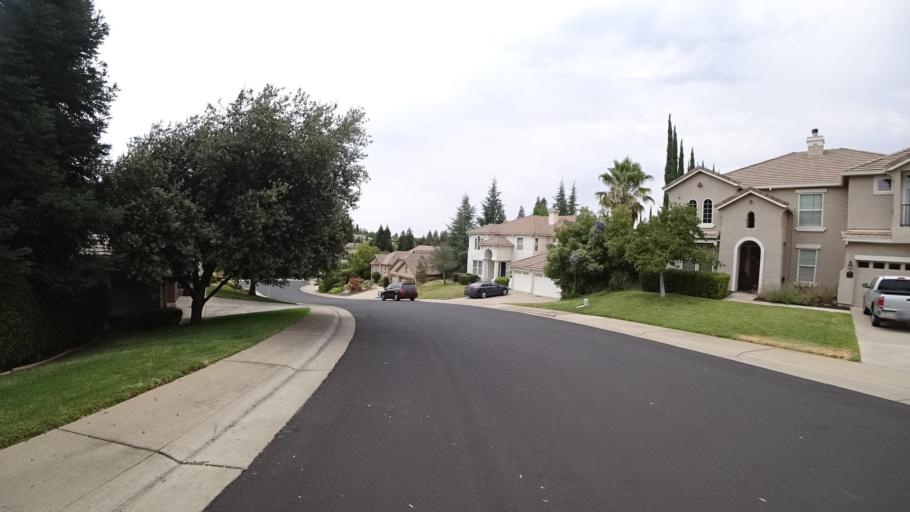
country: US
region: California
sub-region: Placer County
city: Rocklin
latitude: 38.7760
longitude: -121.2189
